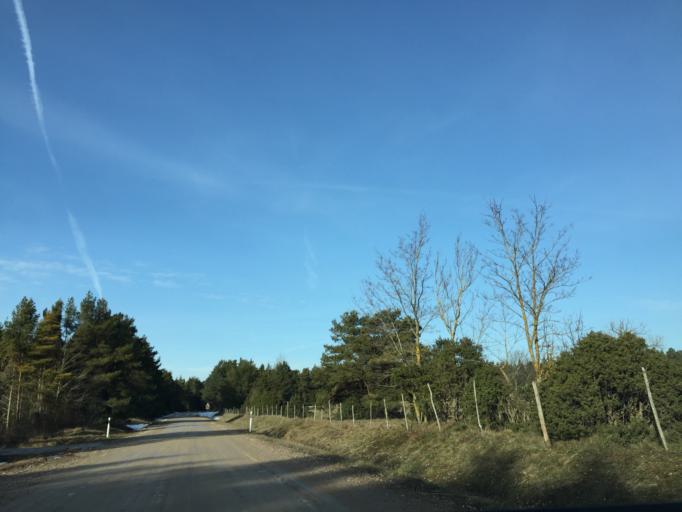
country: EE
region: Saare
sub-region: Kuressaare linn
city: Kuressaare
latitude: 58.3698
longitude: 22.0195
